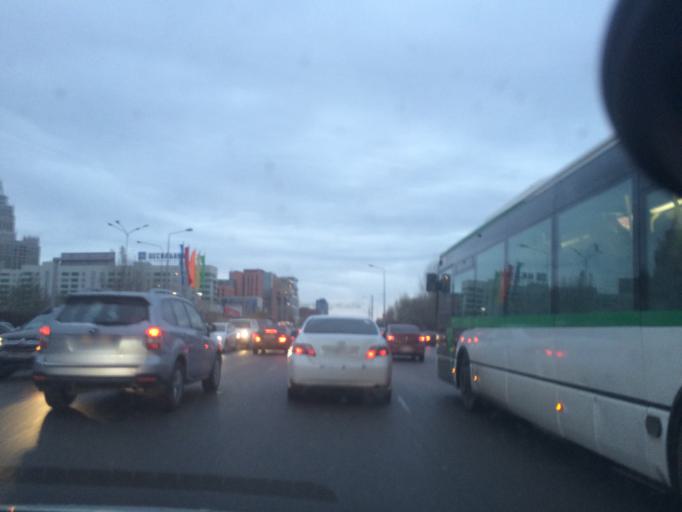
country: KZ
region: Astana Qalasy
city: Astana
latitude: 51.1458
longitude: 71.4118
